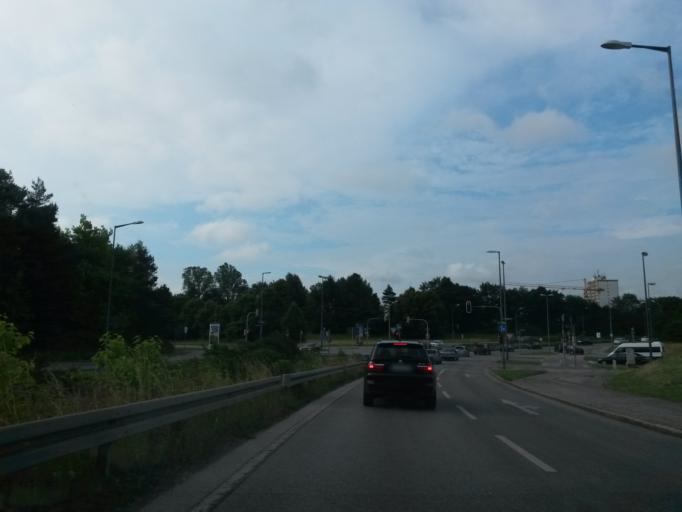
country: DE
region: Bavaria
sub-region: Upper Bavaria
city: Neubiberg
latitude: 48.1053
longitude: 11.6516
